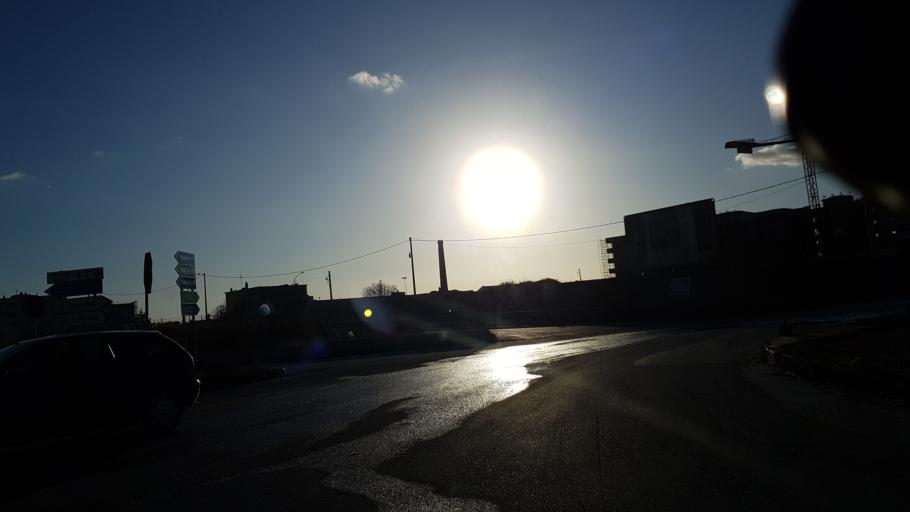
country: IT
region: Apulia
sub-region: Provincia di Bari
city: Gioia del Colle
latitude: 40.8018
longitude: 16.9070
